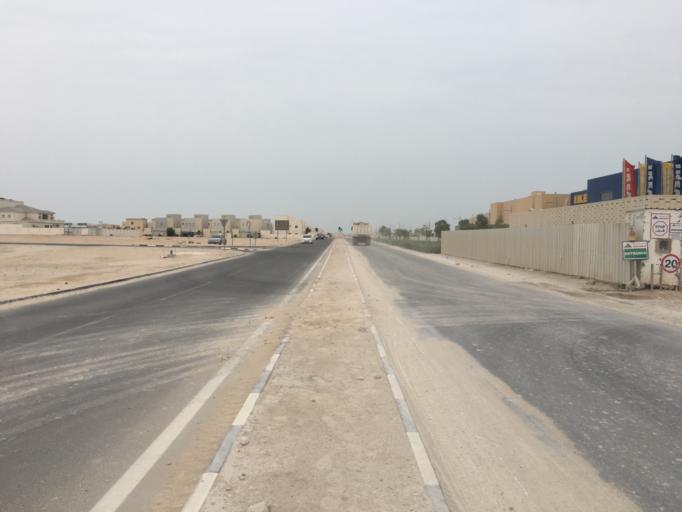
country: QA
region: Baladiyat Umm Salal
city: Umm Salal Muhammad
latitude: 25.3882
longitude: 51.4377
